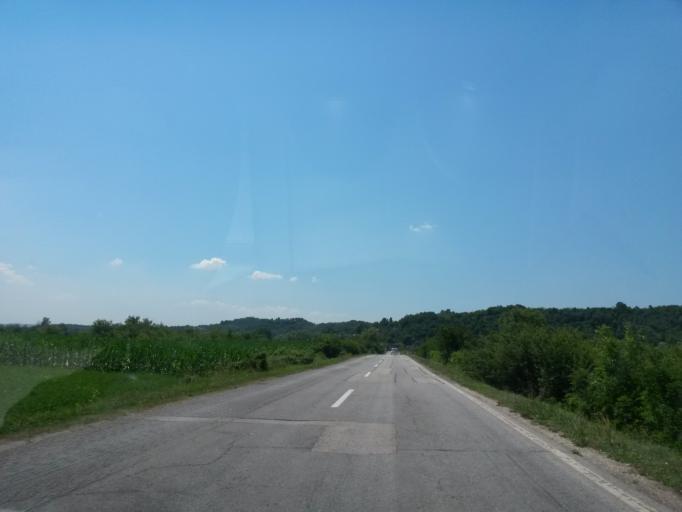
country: BA
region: Republika Srpska
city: Doboj
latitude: 44.8598
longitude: 18.0635
